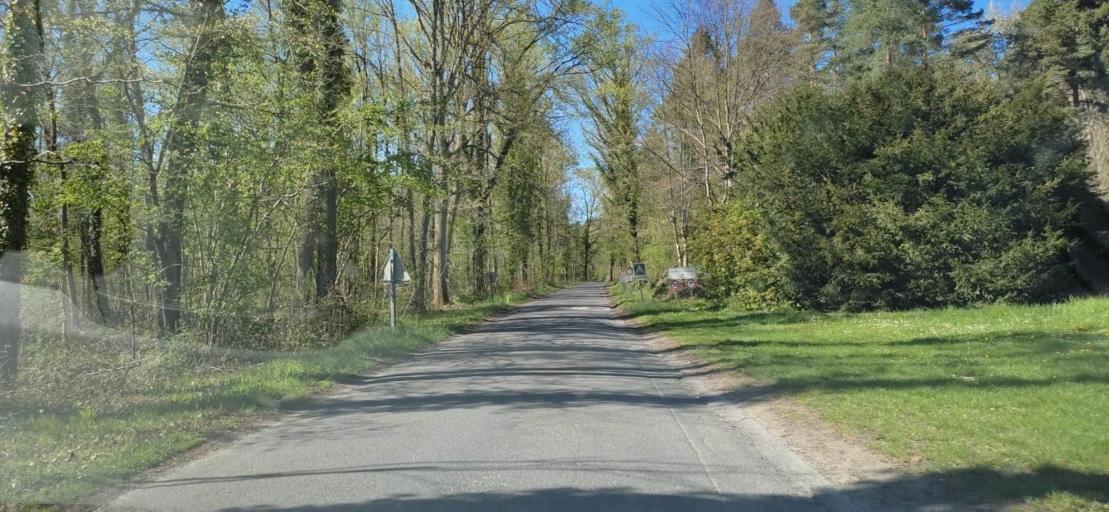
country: FR
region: Picardie
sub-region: Departement de l'Oise
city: Choisy-au-Bac
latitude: 49.4354
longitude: 2.9133
